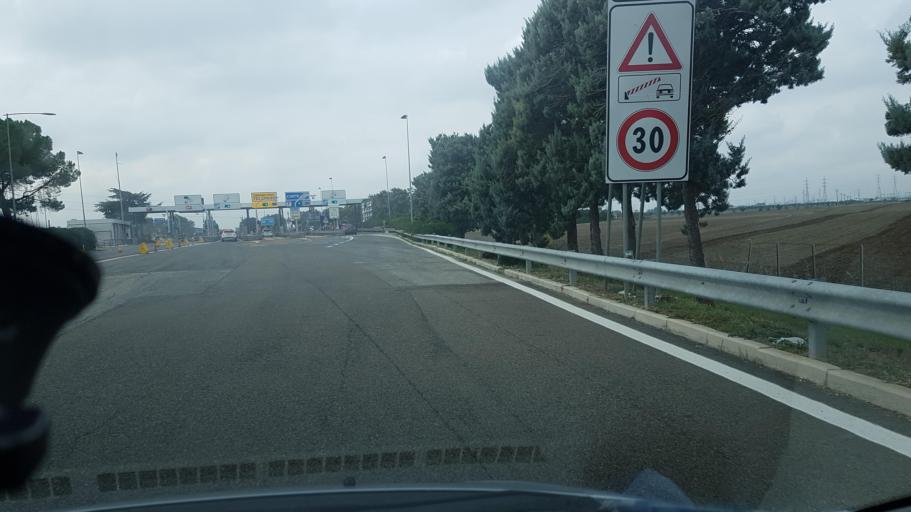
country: IT
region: Apulia
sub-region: Provincia di Foggia
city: Foggia
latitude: 41.4989
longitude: 15.5668
